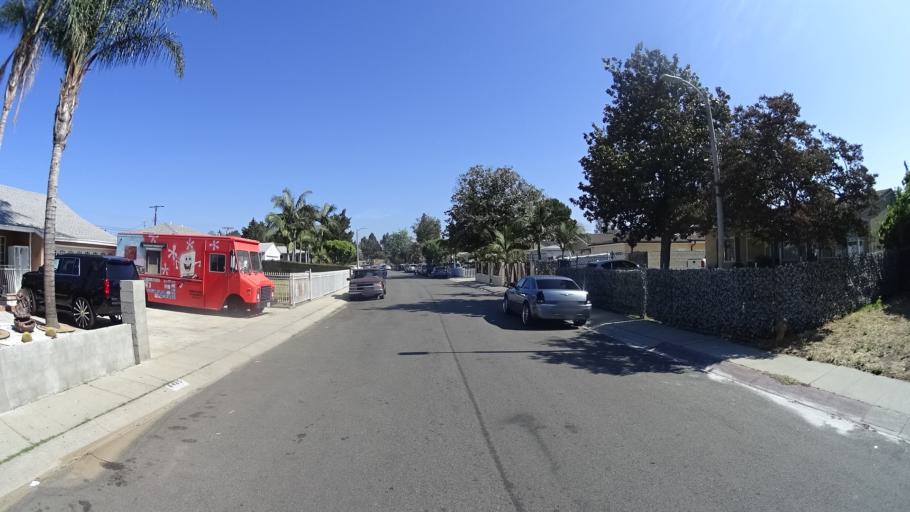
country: US
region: California
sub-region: Los Angeles County
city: Van Nuys
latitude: 34.2242
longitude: -118.4393
